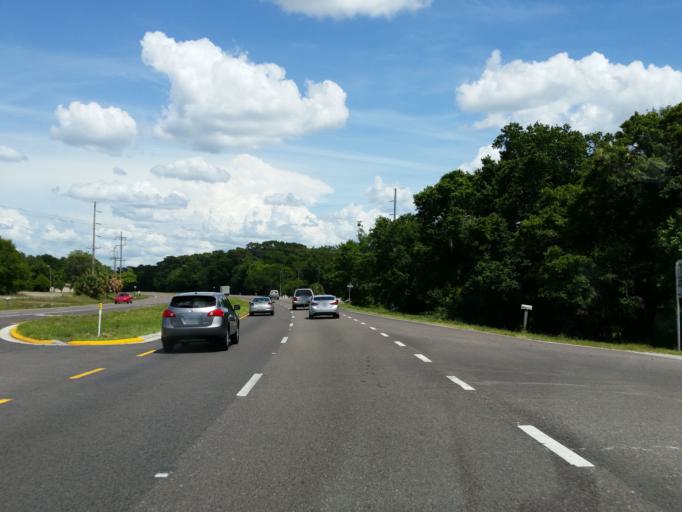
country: US
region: Florida
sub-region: Polk County
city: Willow Oak
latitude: 27.9277
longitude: -82.0750
